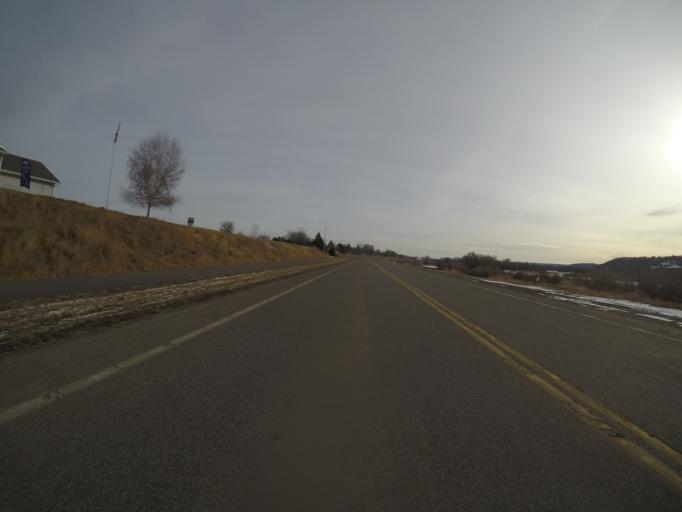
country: US
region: Montana
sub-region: Stillwater County
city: Columbus
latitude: 45.6407
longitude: -109.2694
